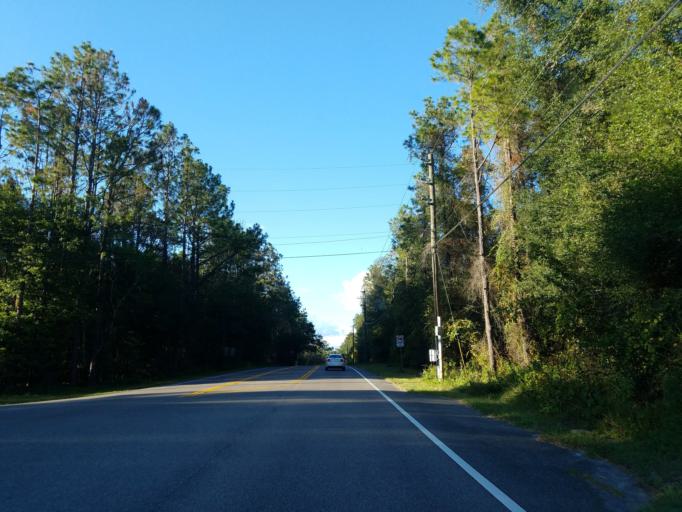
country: US
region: Florida
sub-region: Hernando County
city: Hill 'n Dale
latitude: 28.4715
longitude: -82.3012
